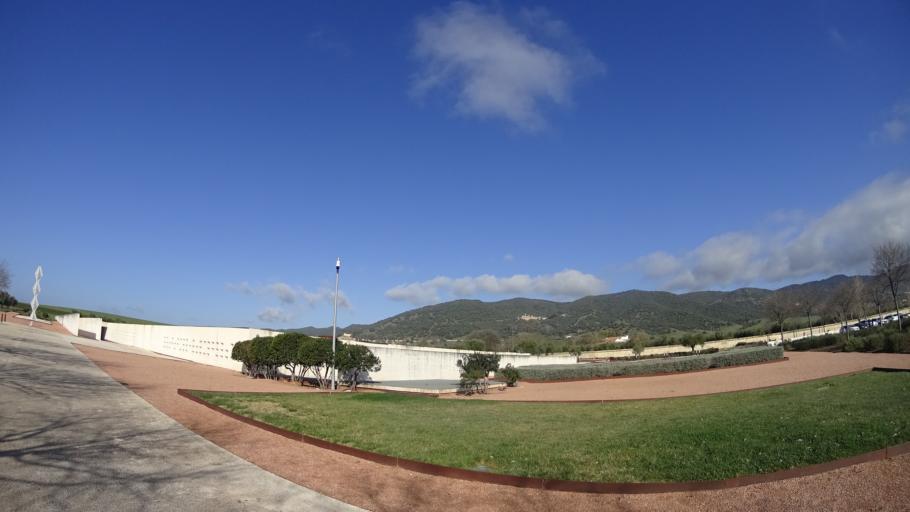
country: ES
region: Andalusia
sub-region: Province of Cordoba
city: Villarrubia
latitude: 37.8807
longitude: -4.8533
